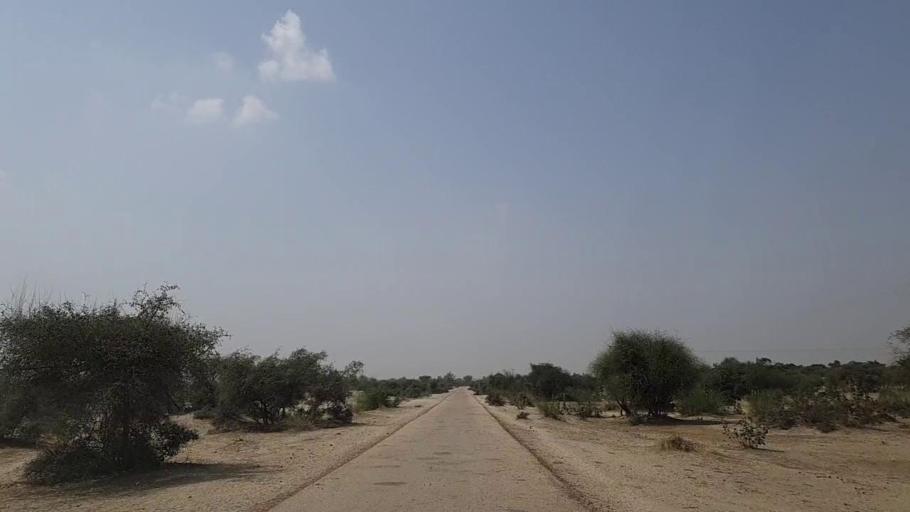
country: PK
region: Sindh
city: Mithi
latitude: 24.7629
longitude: 69.9223
